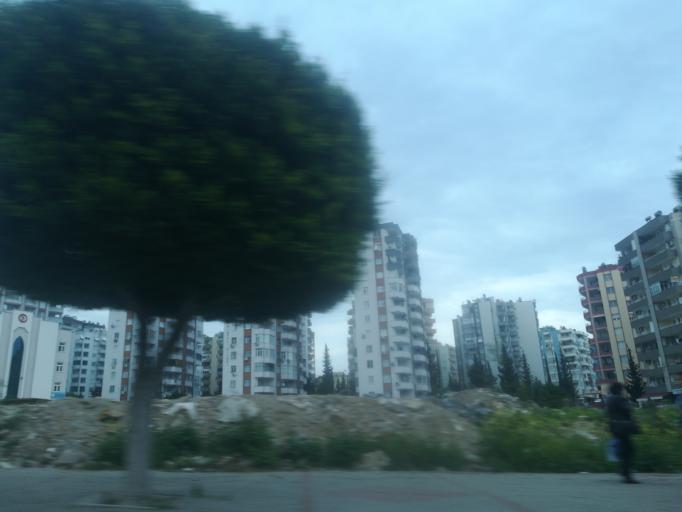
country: TR
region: Adana
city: Adana
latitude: 37.0417
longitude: 35.2921
